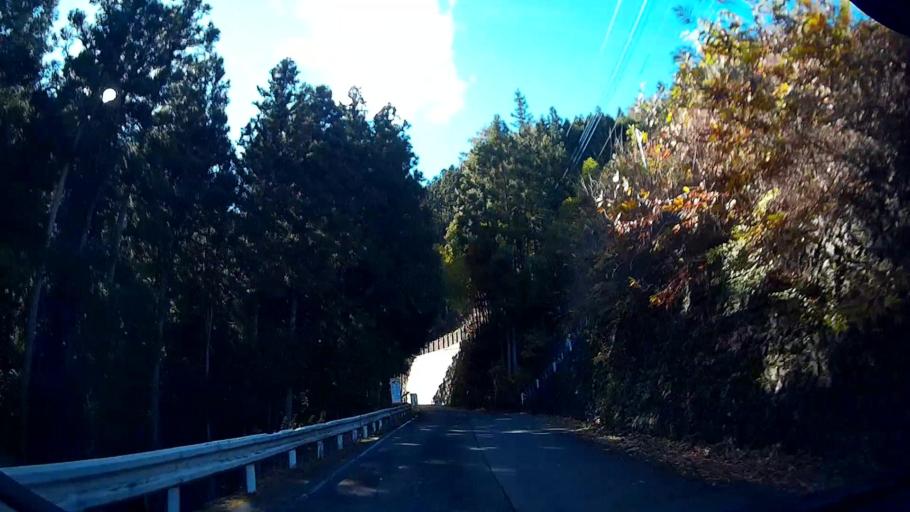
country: JP
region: Yamanashi
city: Otsuki
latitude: 35.7456
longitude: 138.9582
